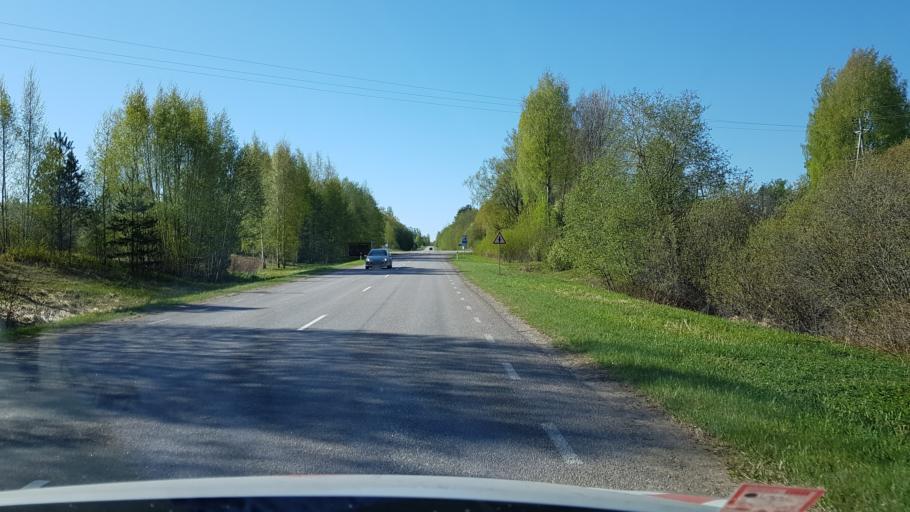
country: EE
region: Vorumaa
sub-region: Voru linn
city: Voru
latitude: 57.7859
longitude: 27.0348
